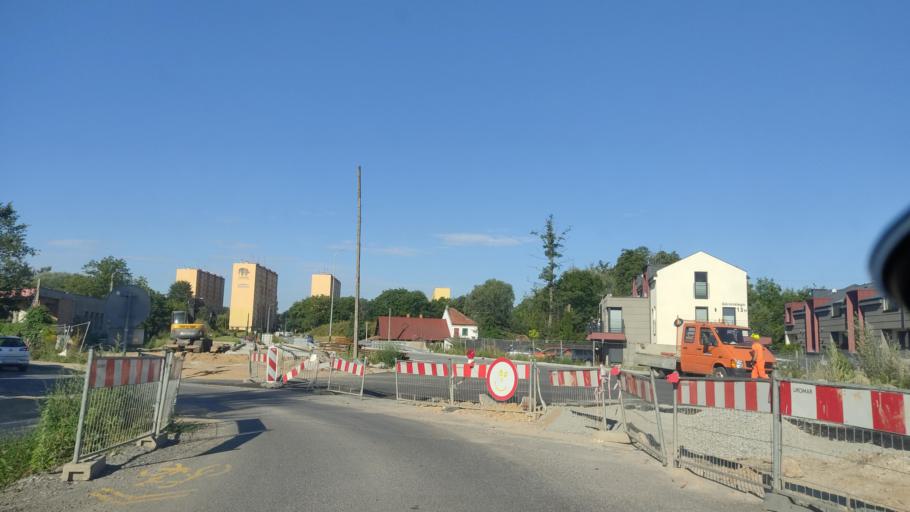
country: PL
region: Lesser Poland Voivodeship
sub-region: Powiat krakowski
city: Zielonki
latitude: 50.0958
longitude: 19.9409
